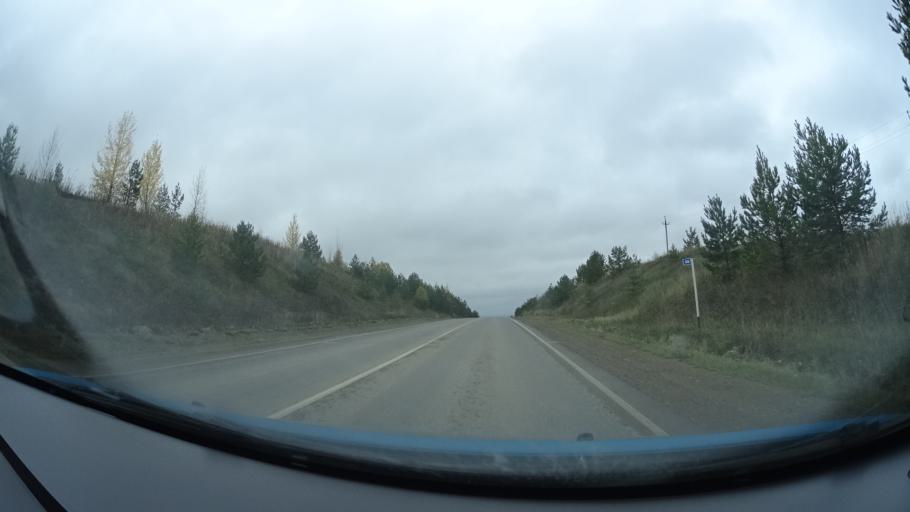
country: RU
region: Perm
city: Osa
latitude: 57.2351
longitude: 55.5946
